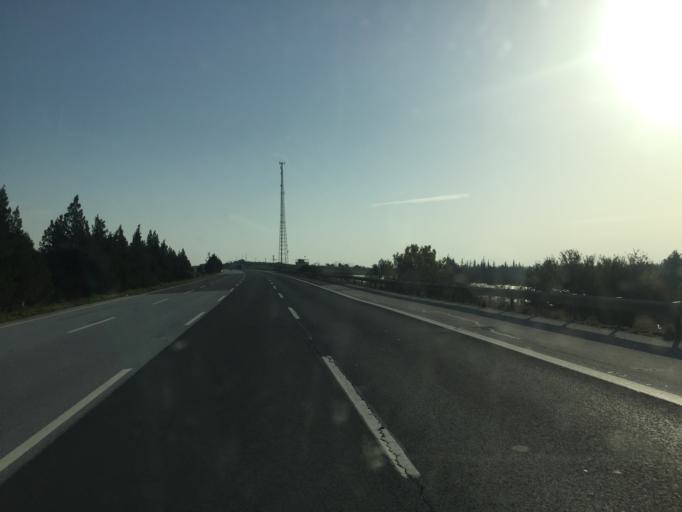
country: TR
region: Mersin
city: Yenice
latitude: 37.0226
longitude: 35.0816
